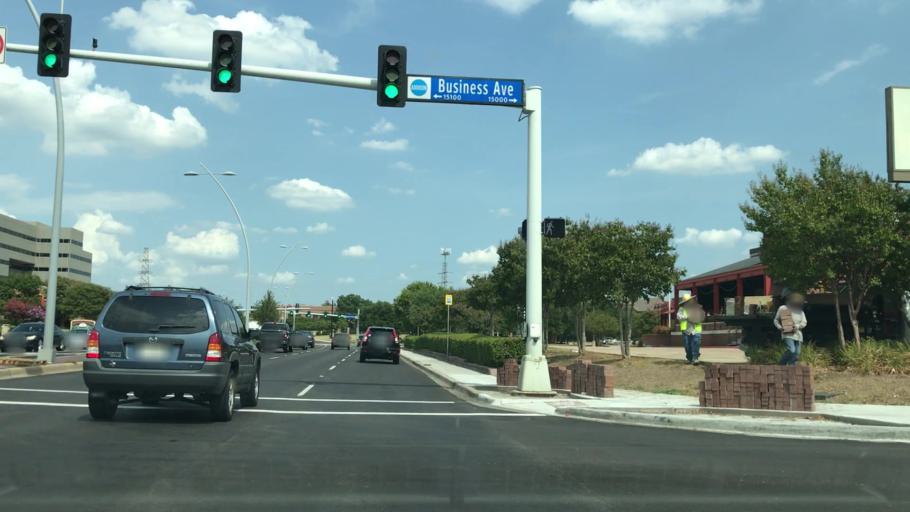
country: US
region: Texas
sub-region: Dallas County
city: Addison
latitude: 32.9531
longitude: -96.8515
